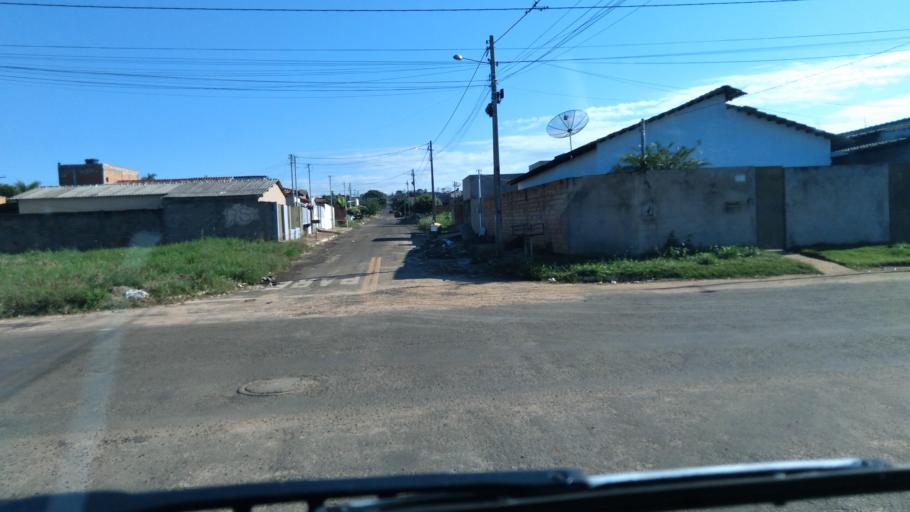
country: BR
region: Goias
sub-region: Mineiros
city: Mineiros
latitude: -17.5766
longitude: -52.5699
